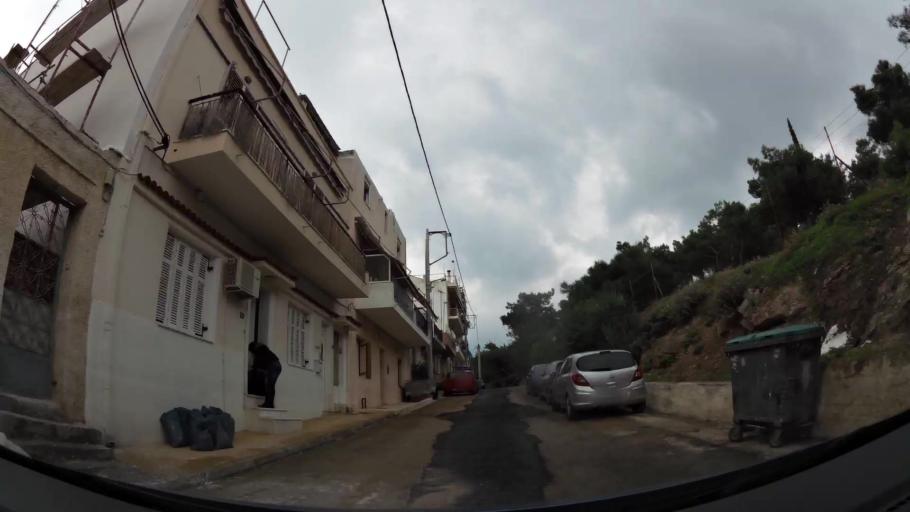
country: GR
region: Attica
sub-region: Nomarchia Athinas
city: Kaisariani
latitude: 37.9640
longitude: 23.7688
